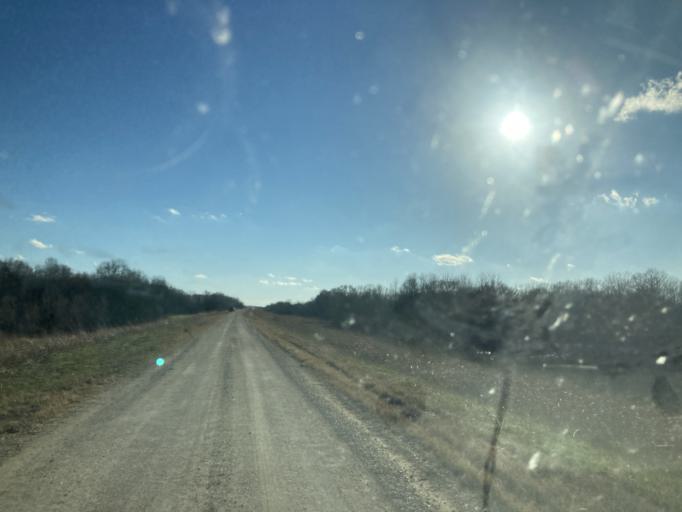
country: US
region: Mississippi
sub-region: Yazoo County
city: Yazoo City
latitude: 32.9247
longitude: -90.5512
